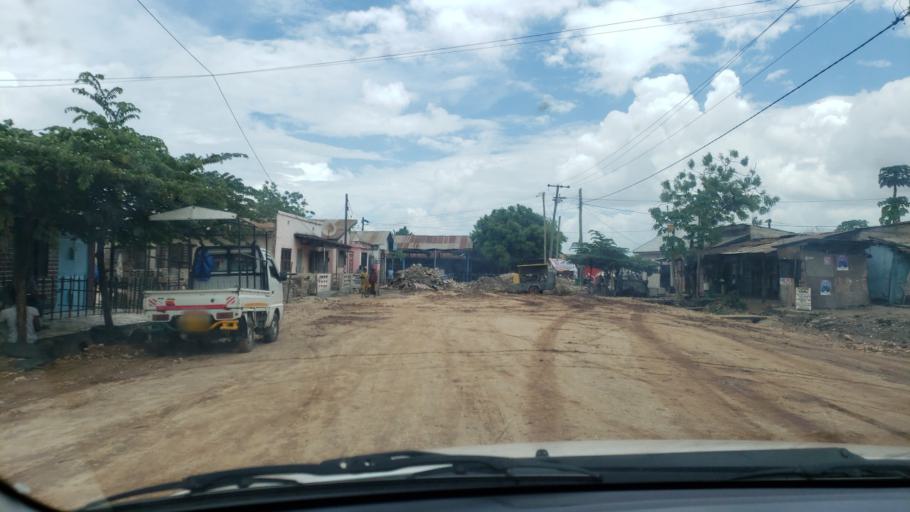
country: TZ
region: Dar es Salaam
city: Magomeni
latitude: -6.8093
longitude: 39.2385
